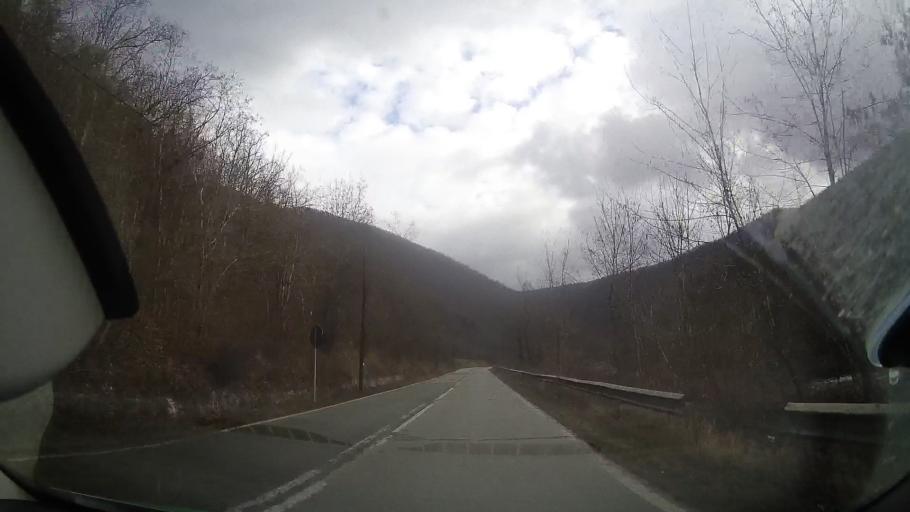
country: RO
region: Alba
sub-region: Comuna Rimetea
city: Rimetea
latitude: 46.5106
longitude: 23.5648
